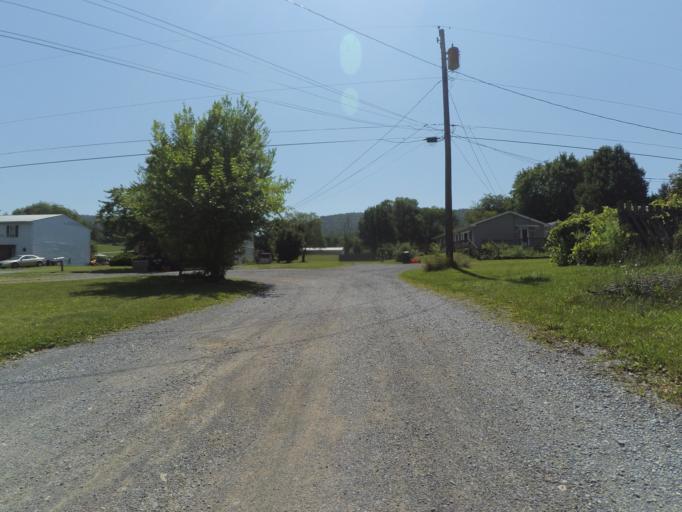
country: US
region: Pennsylvania
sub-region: Centre County
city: Pleasant Gap
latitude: 40.8655
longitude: -77.7485
